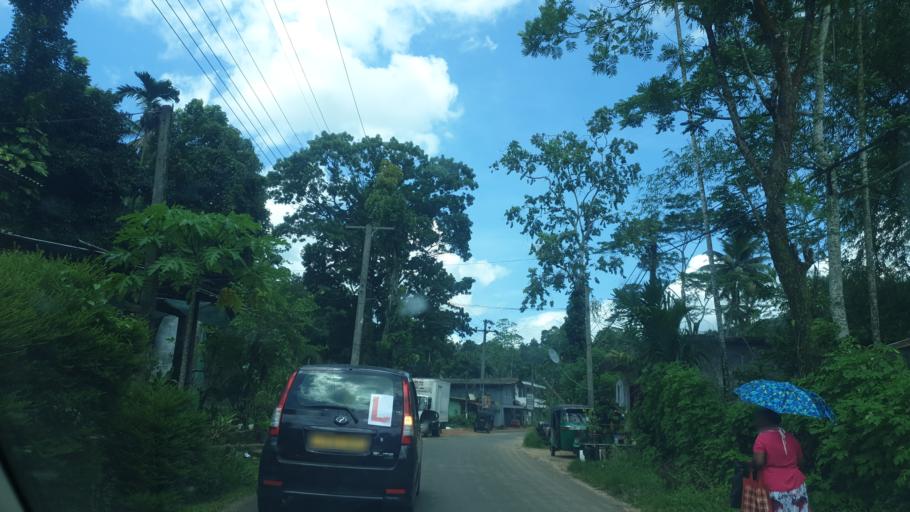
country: LK
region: Sabaragamuwa
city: Ratnapura
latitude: 6.4922
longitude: 80.3978
